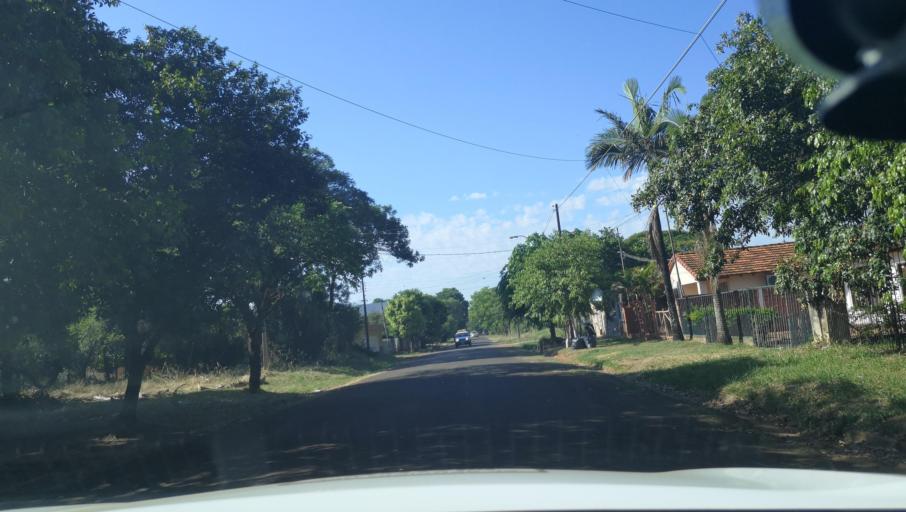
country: PY
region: Itapua
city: Carmen del Parana
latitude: -27.1679
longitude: -56.2359
